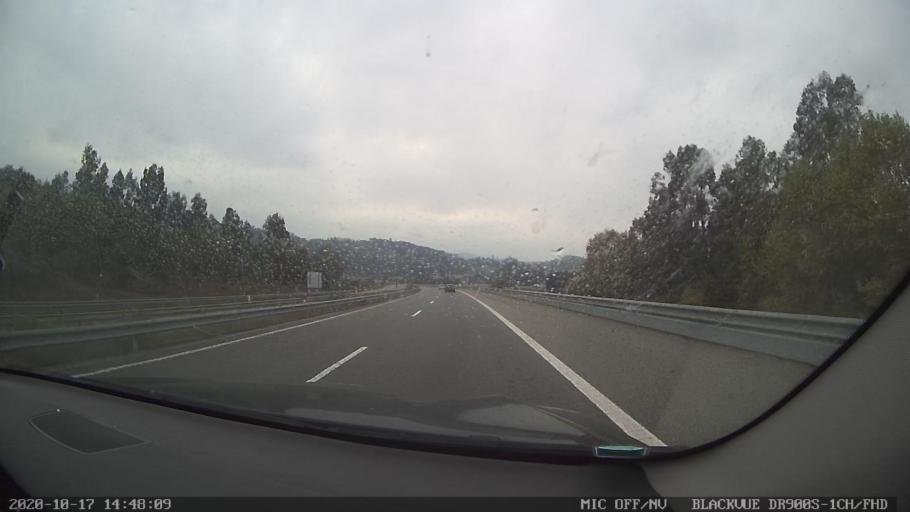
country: PT
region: Braga
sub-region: Barcelos
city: Galegos
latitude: 41.5373
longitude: -8.5380
